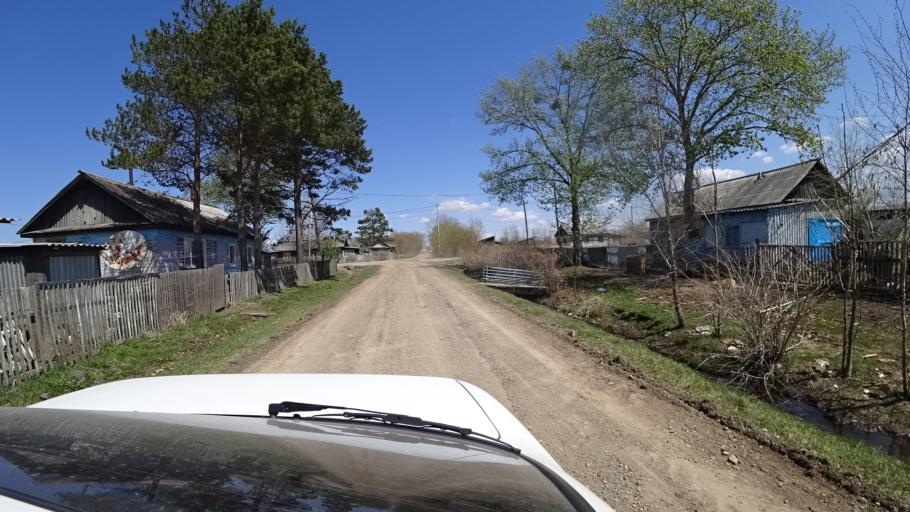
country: RU
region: Primorskiy
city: Dal'nerechensk
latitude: 45.7925
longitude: 133.7718
